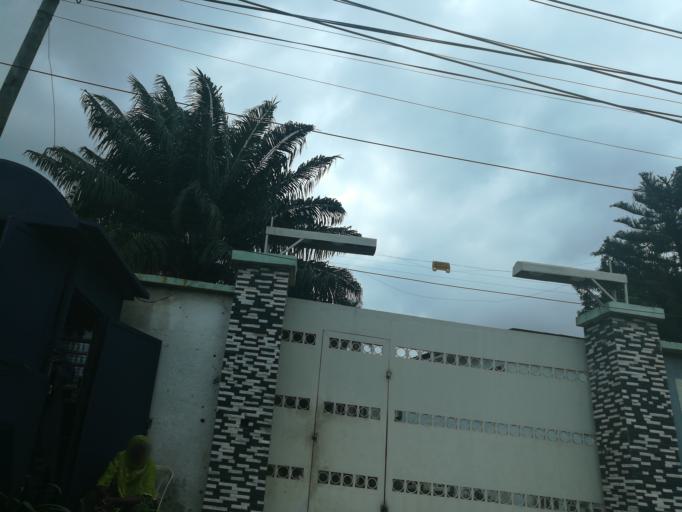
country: NG
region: Lagos
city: Ikeja
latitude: 6.6093
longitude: 3.3439
